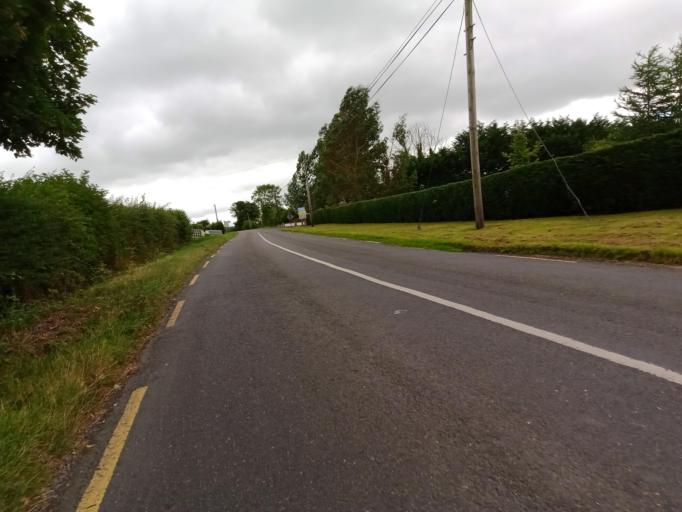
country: IE
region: Leinster
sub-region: Kilkenny
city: Callan
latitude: 52.5687
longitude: -7.4152
